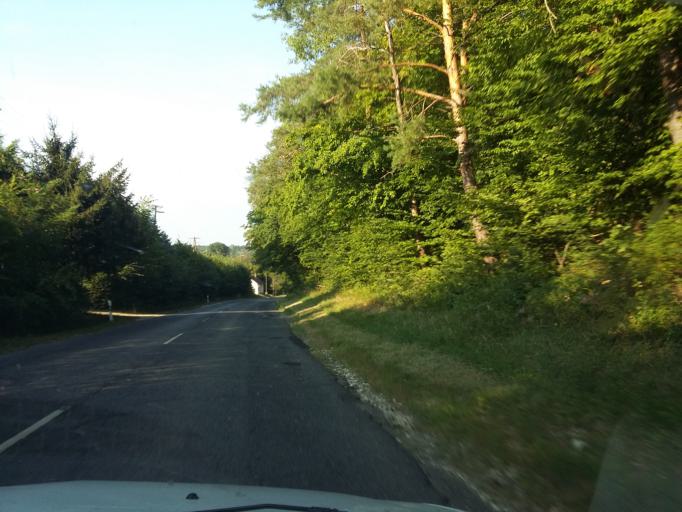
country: SI
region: Hodos-Hodos
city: Hodos
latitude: 46.8355
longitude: 16.4134
